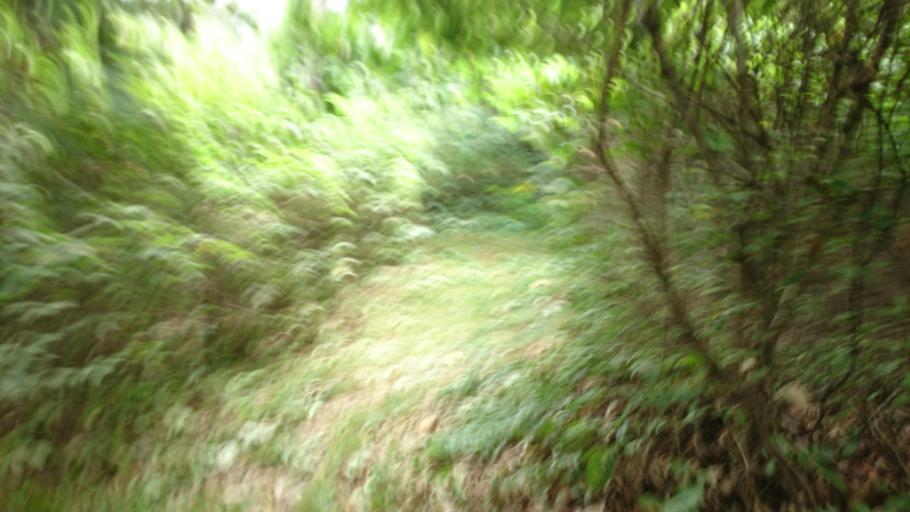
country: KR
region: Daegu
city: Hwawon
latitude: 35.7034
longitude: 128.3449
